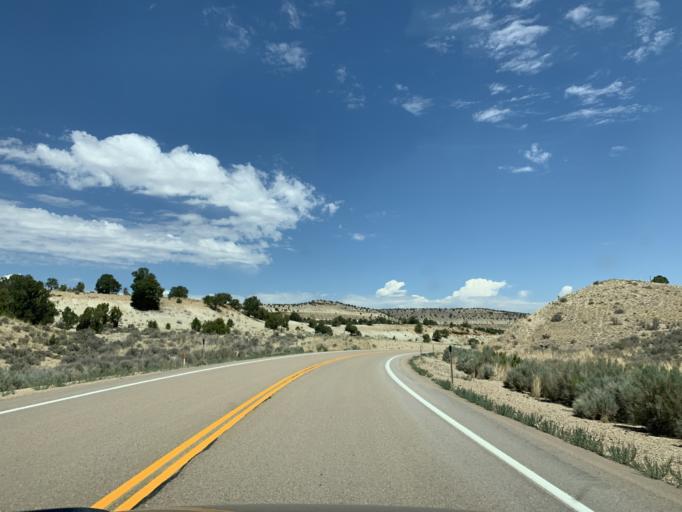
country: US
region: Utah
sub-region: Duchesne County
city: Duchesne
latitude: 39.9561
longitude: -110.1907
